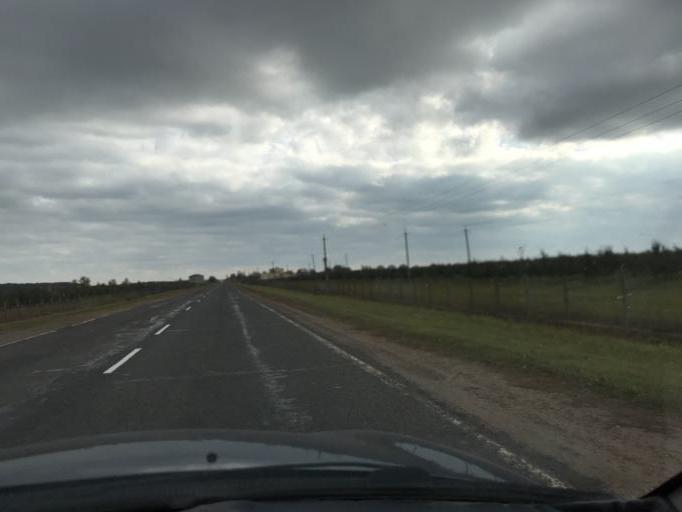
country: BY
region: Grodnenskaya
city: Lida
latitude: 53.7987
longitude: 25.1323
